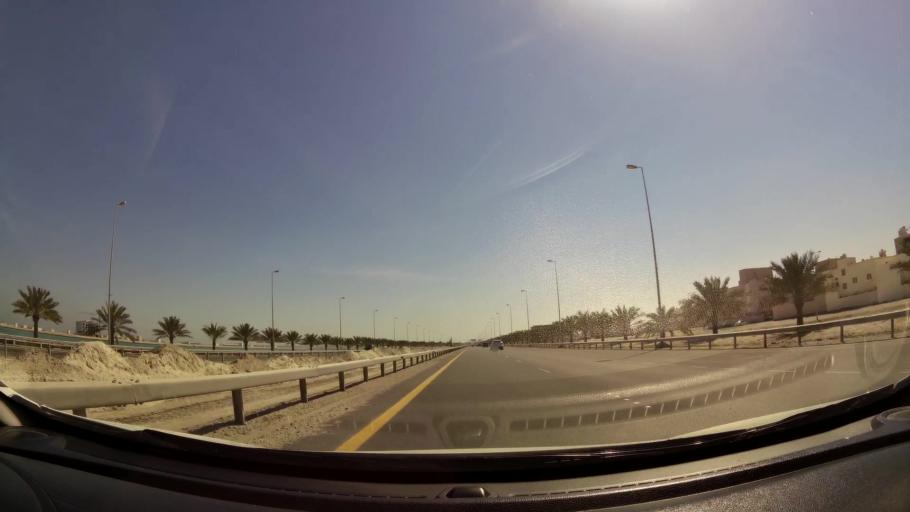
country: BH
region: Muharraq
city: Al Hadd
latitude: 26.2660
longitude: 50.6615
